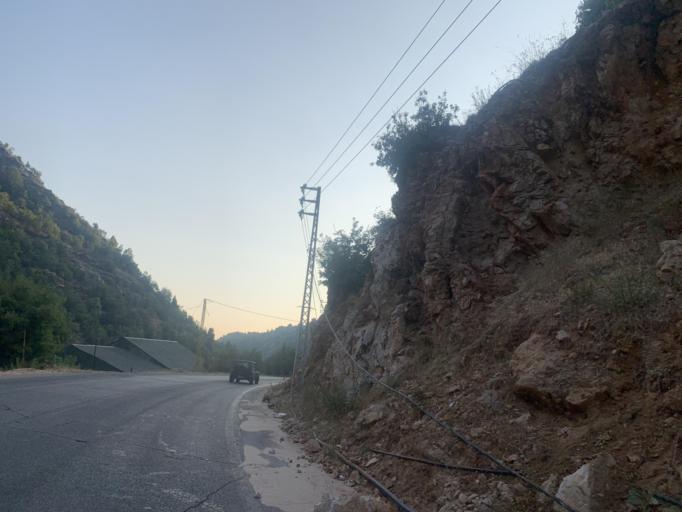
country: LB
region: Liban-Nord
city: Amioun
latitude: 34.1335
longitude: 35.8204
